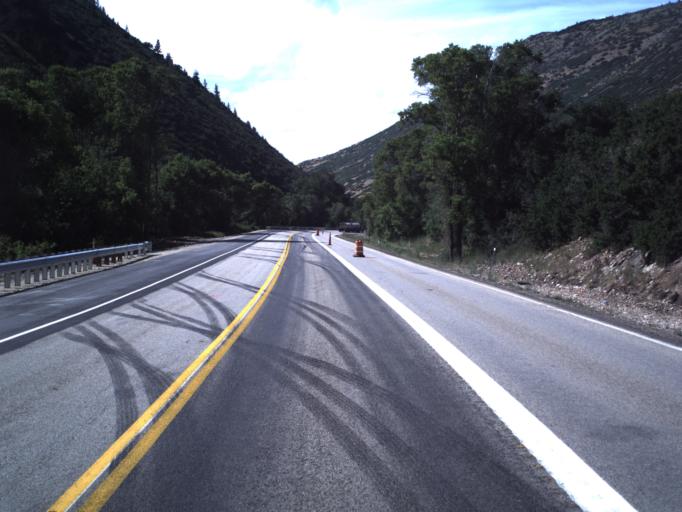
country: US
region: Utah
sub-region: Wasatch County
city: Heber
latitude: 40.4011
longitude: -111.3061
